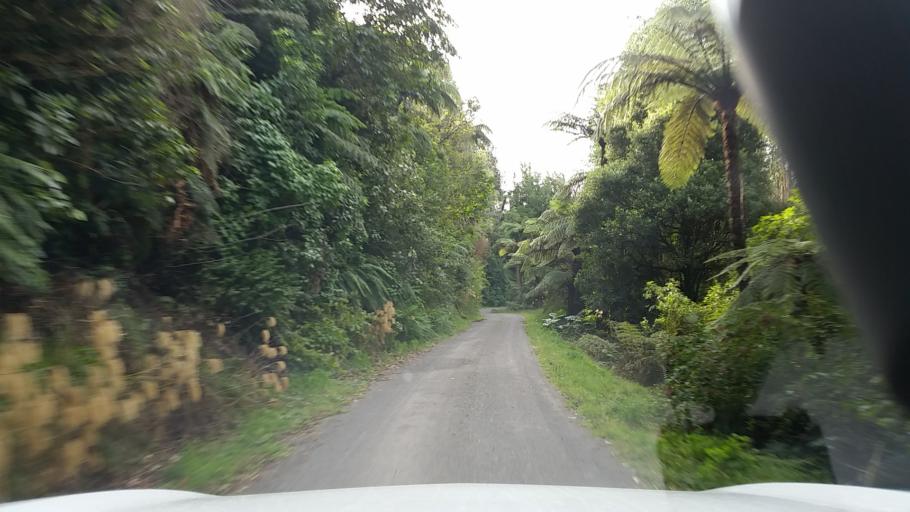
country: NZ
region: Bay of Plenty
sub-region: Rotorua District
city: Rotorua
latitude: -37.9654
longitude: 176.3060
